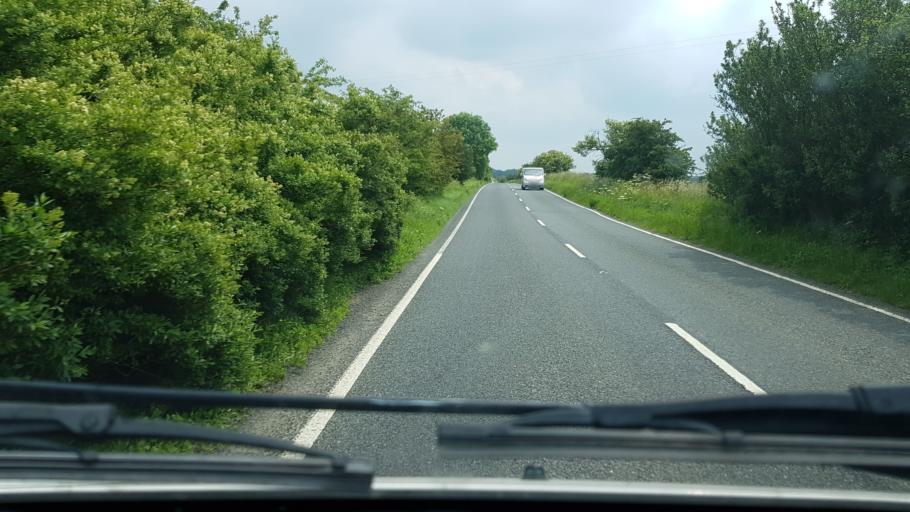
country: GB
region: England
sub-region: Gloucestershire
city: Chipping Campden
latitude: 51.9936
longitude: -1.7790
